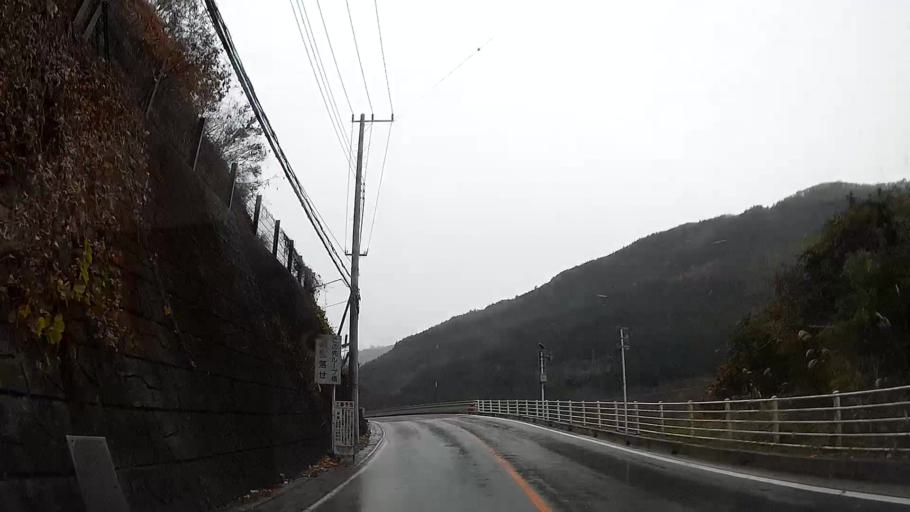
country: JP
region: Saitama
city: Chichibu
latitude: 35.9592
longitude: 138.9027
